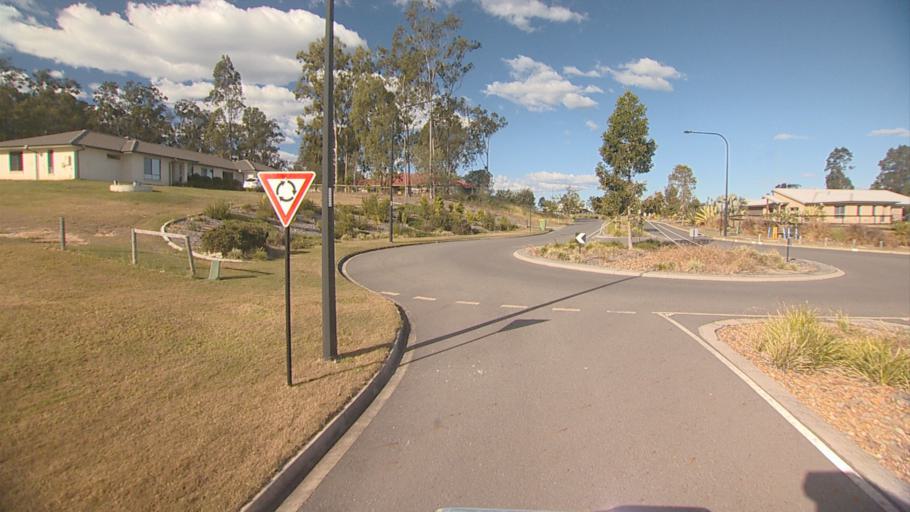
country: AU
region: Queensland
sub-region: Logan
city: North Maclean
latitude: -27.8247
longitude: 152.9780
